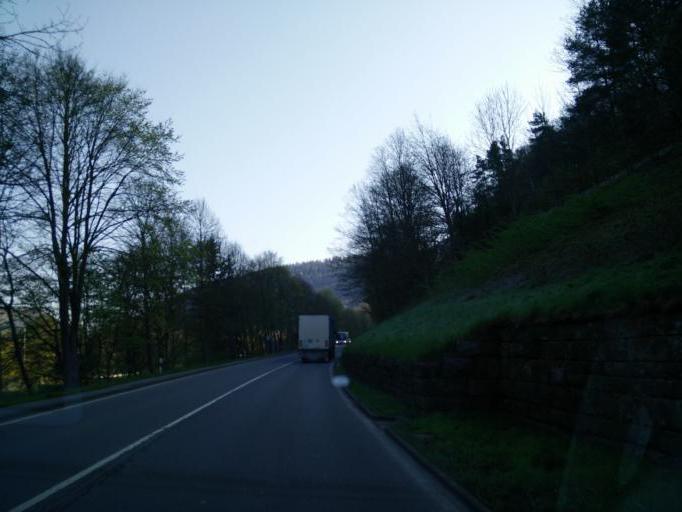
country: DE
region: Baden-Wuerttemberg
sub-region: Karlsruhe Region
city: Calw
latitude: 48.7302
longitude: 8.7335
